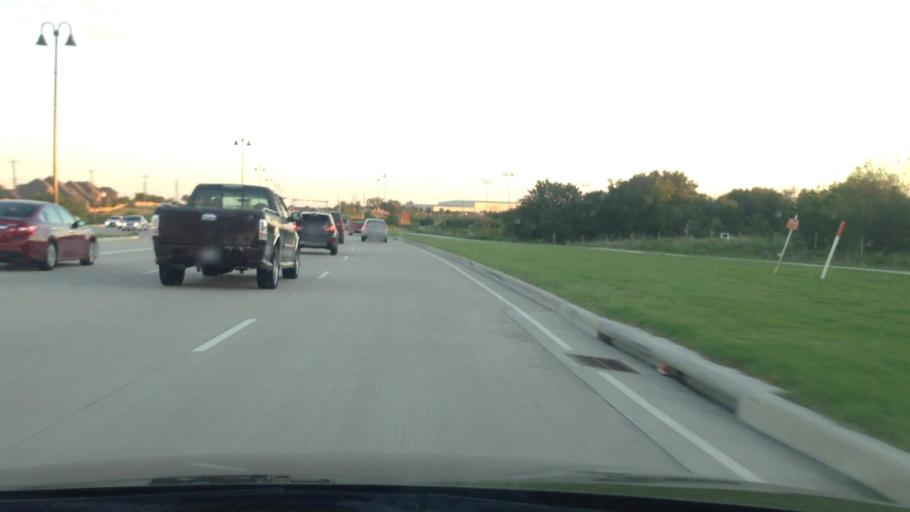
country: US
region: Texas
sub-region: Denton County
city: The Colony
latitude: 33.1190
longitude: -96.8921
